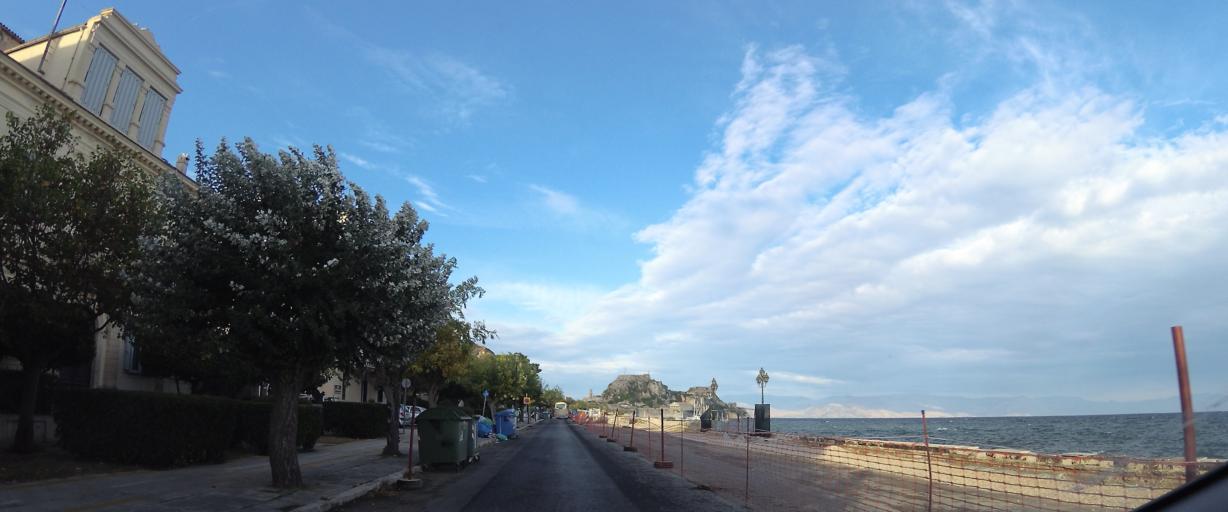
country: GR
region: Ionian Islands
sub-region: Nomos Kerkyras
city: Kerkyra
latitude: 39.6173
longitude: 19.9216
